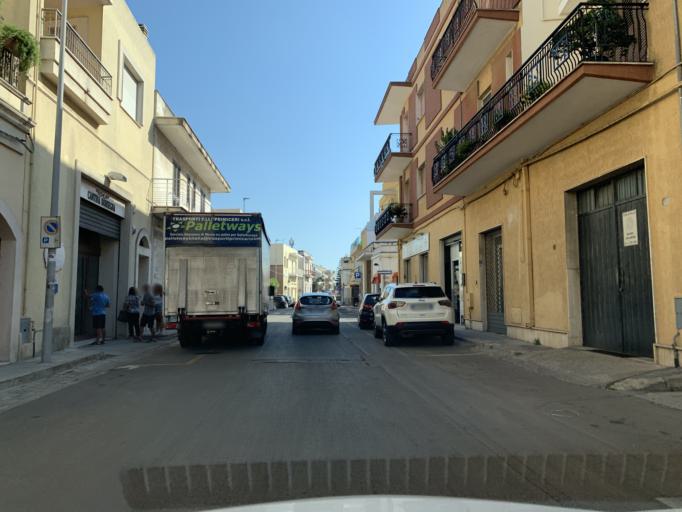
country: IT
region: Apulia
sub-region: Provincia di Lecce
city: Nardo
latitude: 40.1750
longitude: 18.0303
